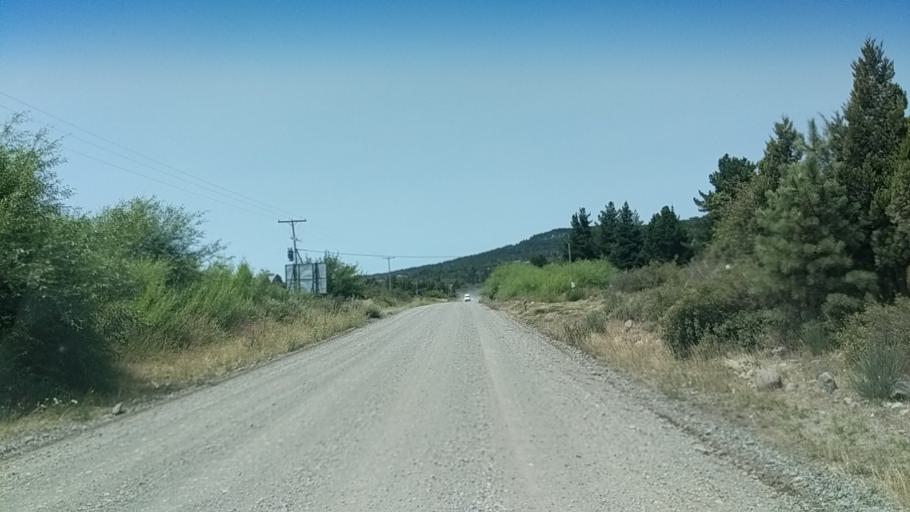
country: AR
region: Chubut
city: Trevelin
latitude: -43.1946
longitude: -71.5885
